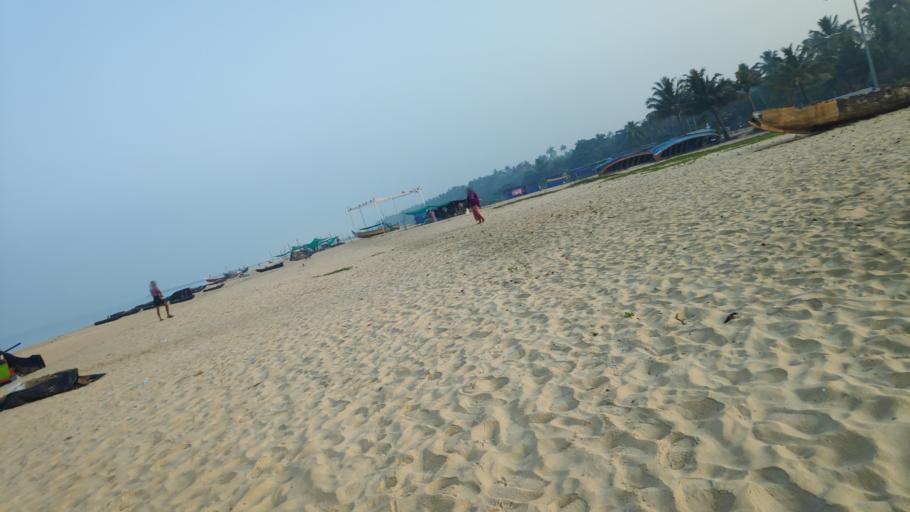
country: IN
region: Kerala
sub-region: Alappuzha
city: Vayalar
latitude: 9.6597
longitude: 76.2921
